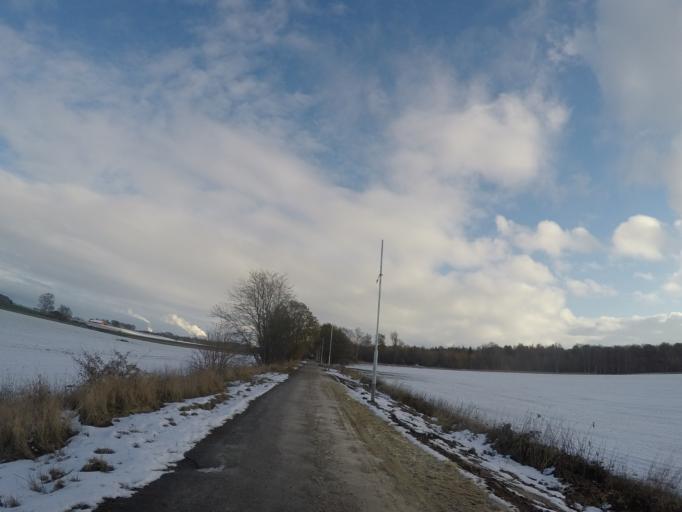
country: SE
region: Skane
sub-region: Lunds Kommun
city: Lund
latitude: 55.7875
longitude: 13.2131
